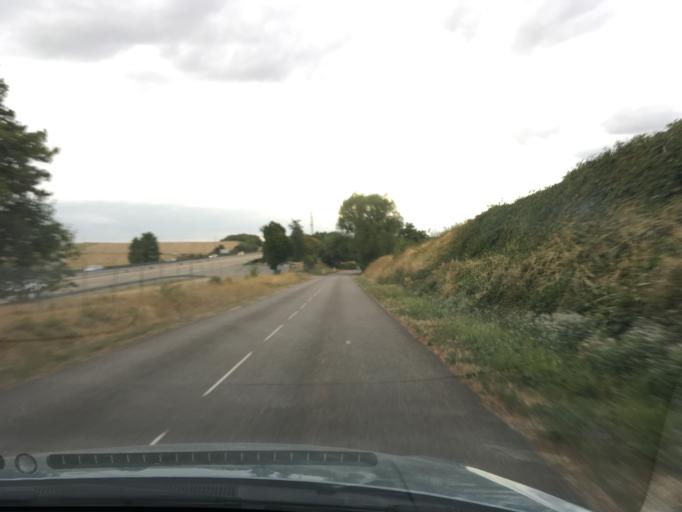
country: FR
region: Bourgogne
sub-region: Departement de l'Yonne
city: Fleury-la-Vallee
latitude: 47.8729
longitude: 3.4821
